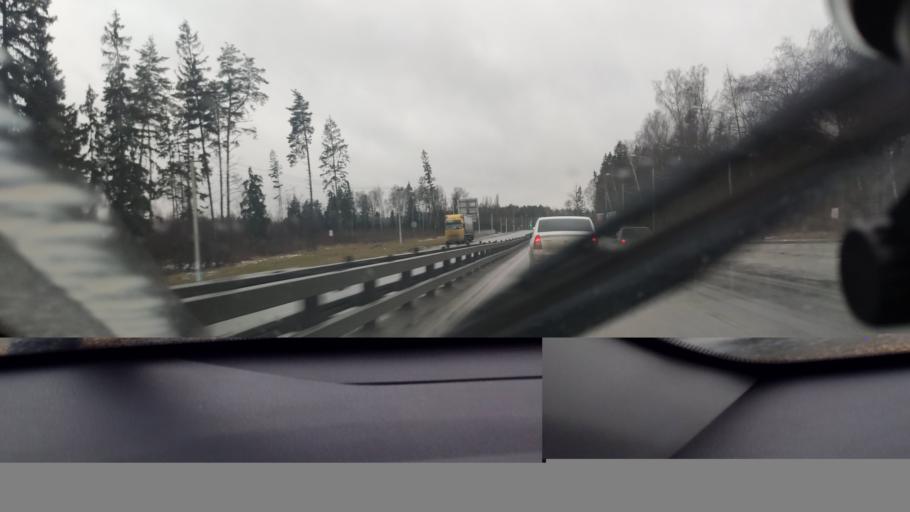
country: RU
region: Moskovskaya
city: Dubrovitsy
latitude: 55.3730
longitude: 37.3904
